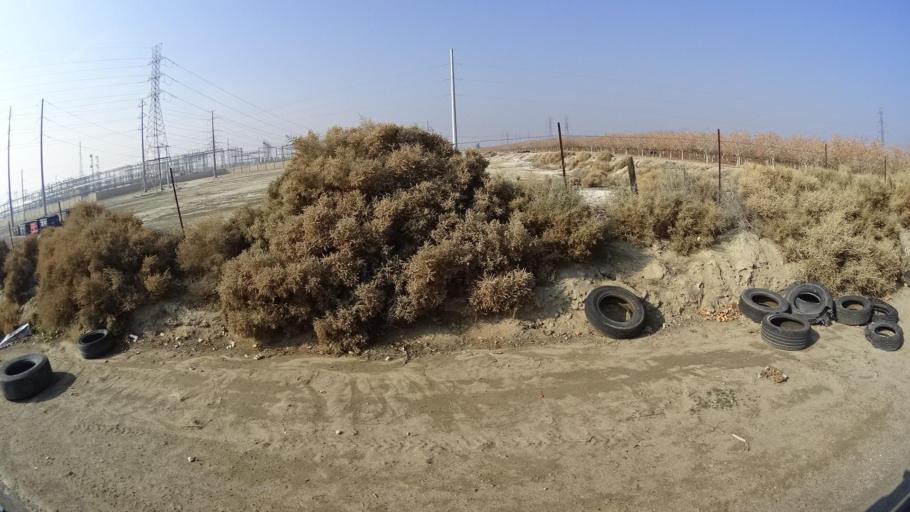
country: US
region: California
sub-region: Kern County
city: Buttonwillow
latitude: 35.4059
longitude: -119.4476
